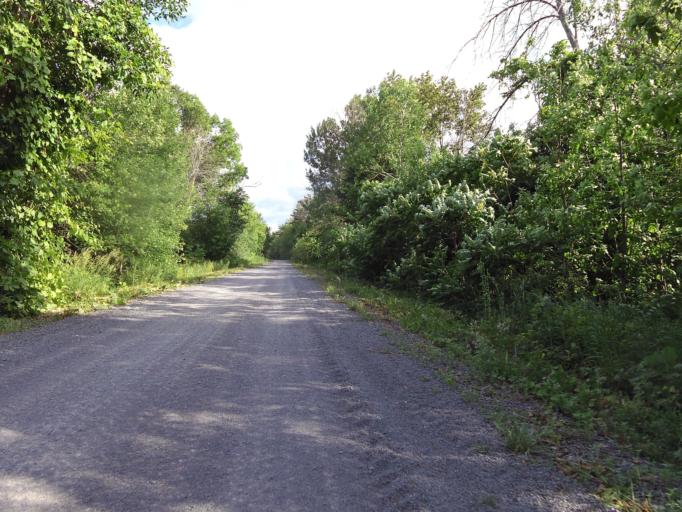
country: CA
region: Ontario
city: Arnprior
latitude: 45.3182
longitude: -76.2854
